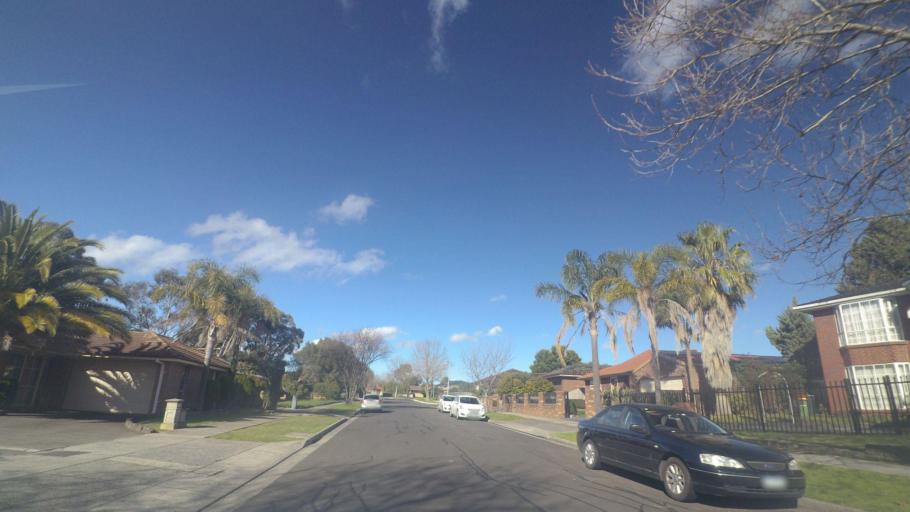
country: AU
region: Victoria
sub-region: Knox
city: Knoxfield
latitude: -37.9136
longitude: 145.2561
